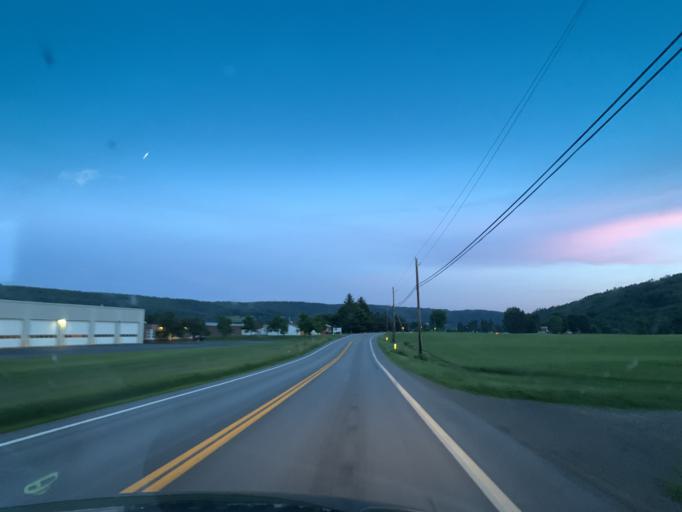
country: US
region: New York
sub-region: Chenango County
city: New Berlin
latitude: 42.5865
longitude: -75.3352
